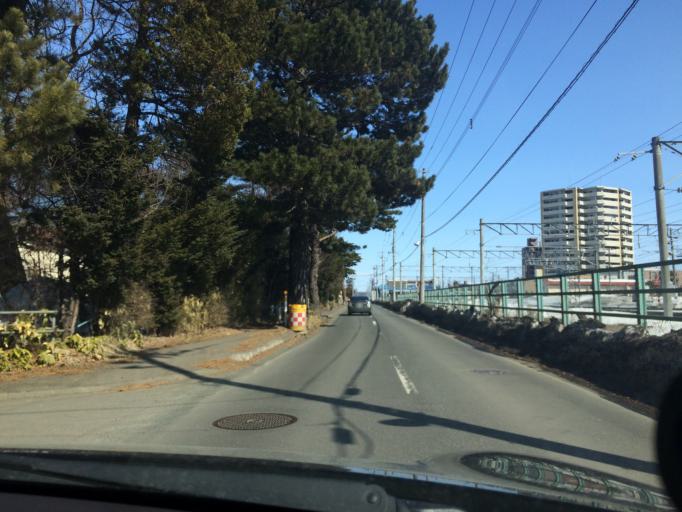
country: JP
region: Hokkaido
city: Ebetsu
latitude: 43.0442
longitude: 141.4601
